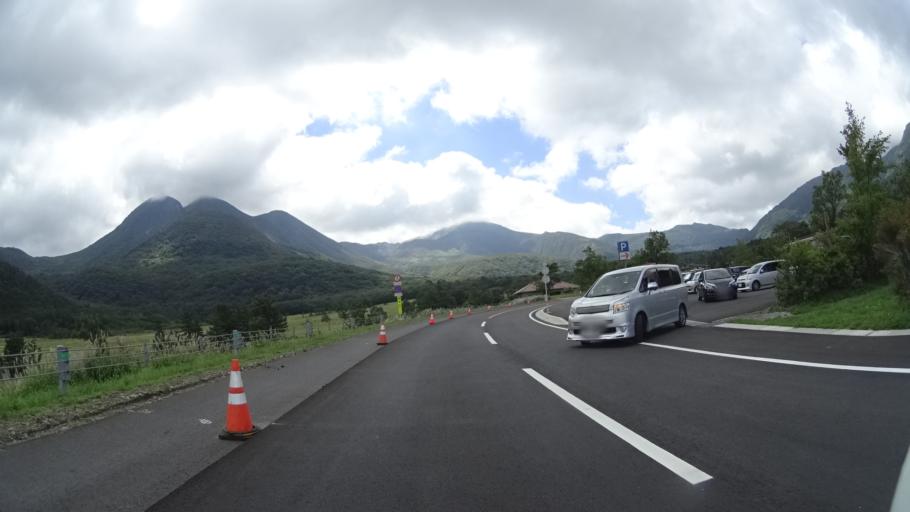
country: JP
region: Oita
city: Tsukawaki
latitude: 33.1204
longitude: 131.2307
